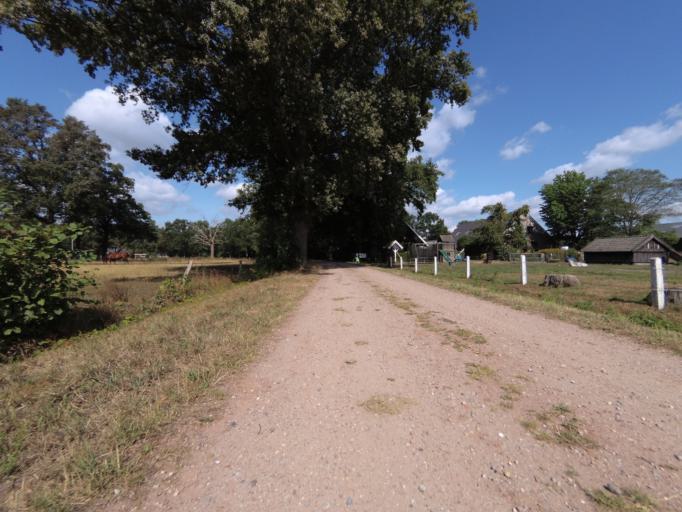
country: NL
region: Overijssel
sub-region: Gemeente Hengelo
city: Hengelo
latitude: 52.2564
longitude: 6.8356
